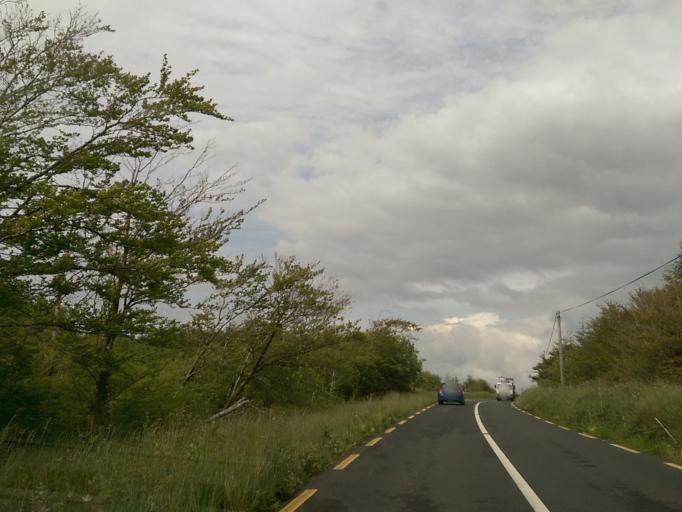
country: IE
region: Connaught
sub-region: County Galway
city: Bearna
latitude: 53.0584
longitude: -9.2070
